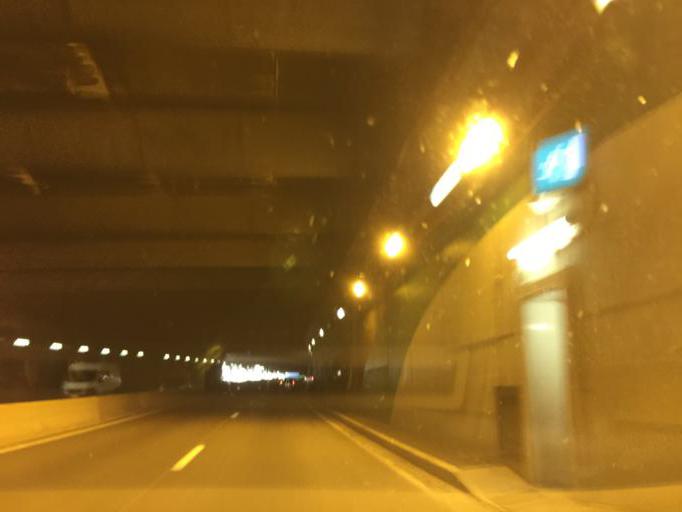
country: FR
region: Rhone-Alpes
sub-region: Departement de la Loire
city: Firminy
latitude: 45.3913
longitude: 4.2870
